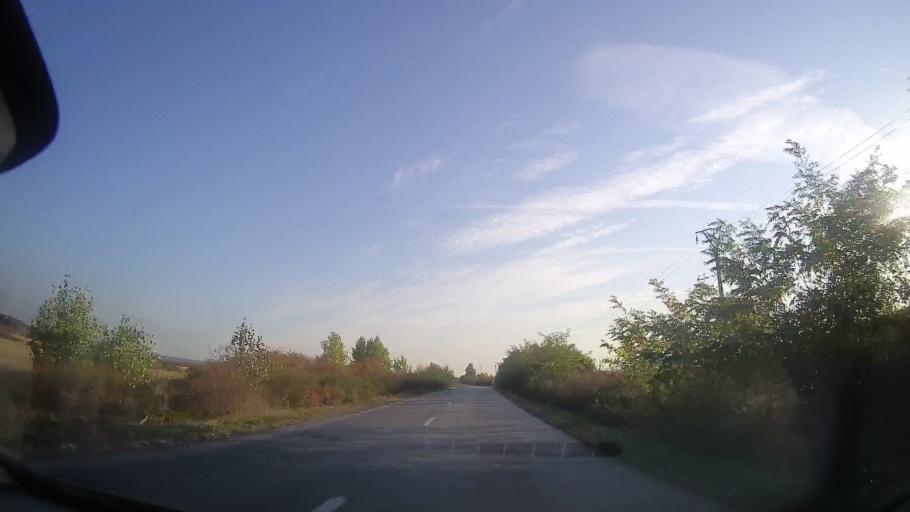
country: RO
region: Timis
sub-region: Comuna Pischia
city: Pischia
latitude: 45.8774
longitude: 21.3326
